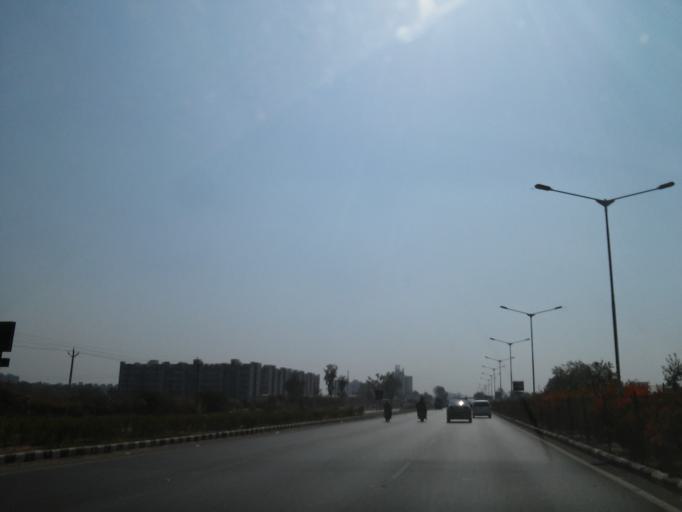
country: IN
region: Gujarat
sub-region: Gandhinagar
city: Adalaj
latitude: 23.1127
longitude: 72.5359
